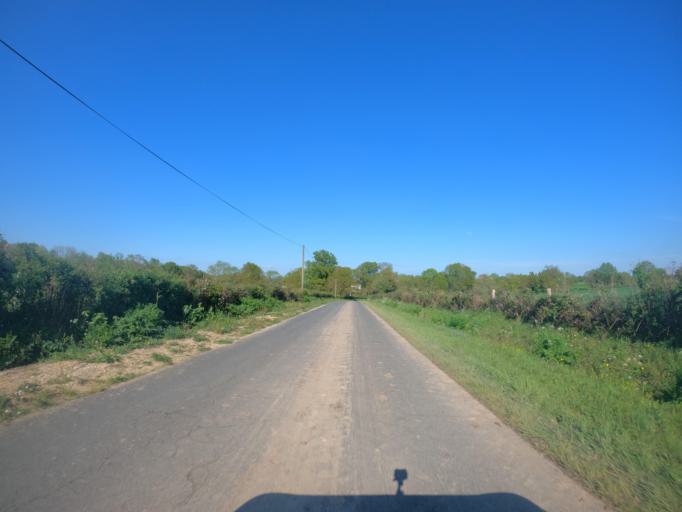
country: FR
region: Poitou-Charentes
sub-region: Departement des Deux-Sevres
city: La Chapelle-Saint-Laurent
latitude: 46.6823
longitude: -0.5217
